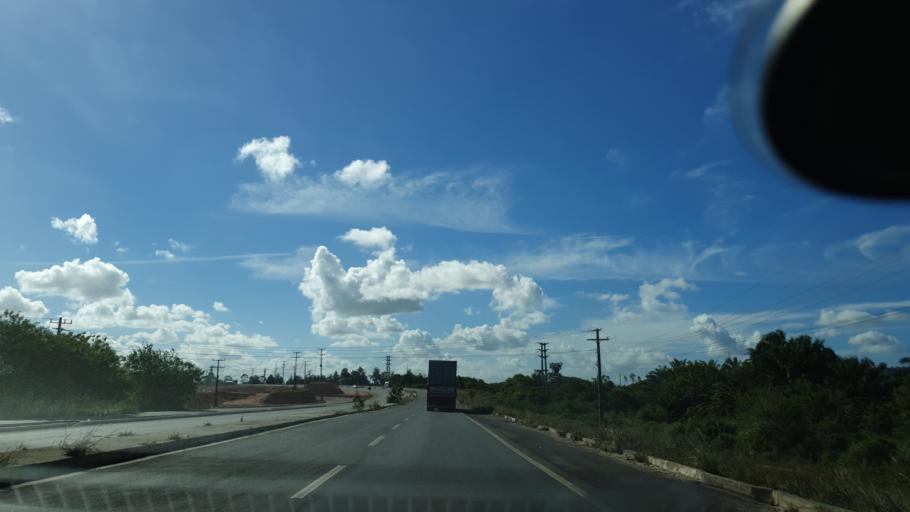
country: BR
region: Bahia
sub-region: Camacari
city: Camacari
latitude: -12.6843
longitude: -38.2631
